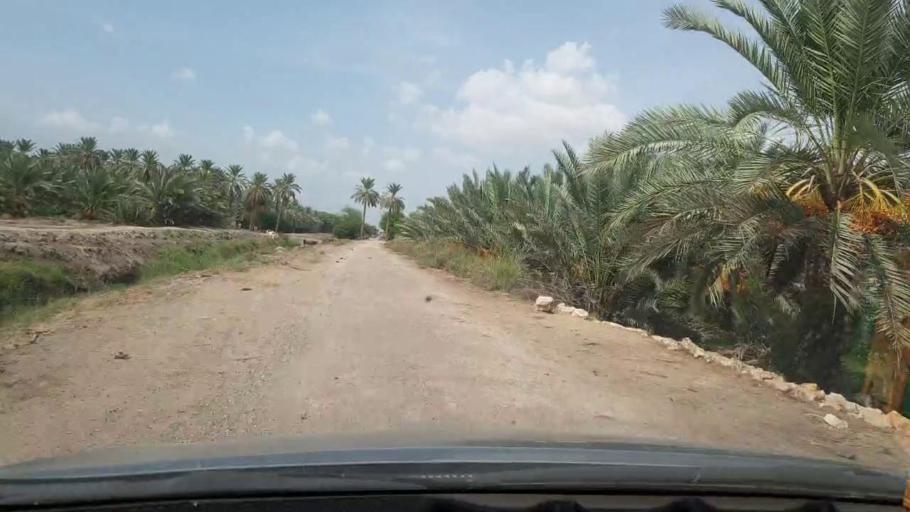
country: PK
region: Sindh
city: Khairpur
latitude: 27.5203
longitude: 68.8833
